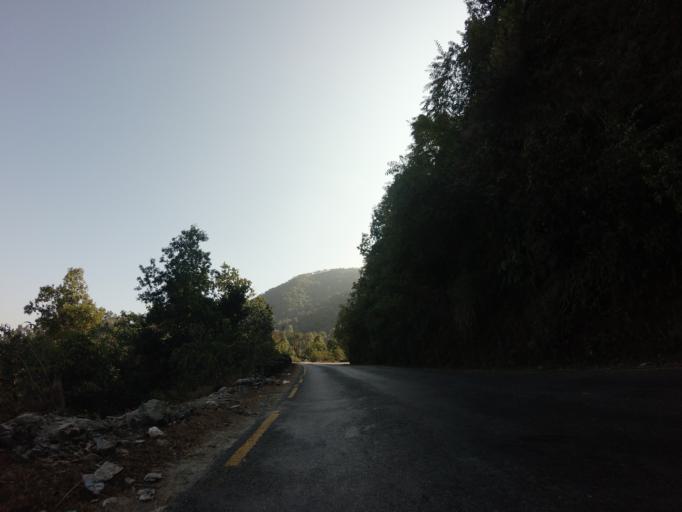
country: NP
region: Western Region
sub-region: Gandaki Zone
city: Pokhara
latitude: 28.1901
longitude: 83.9006
